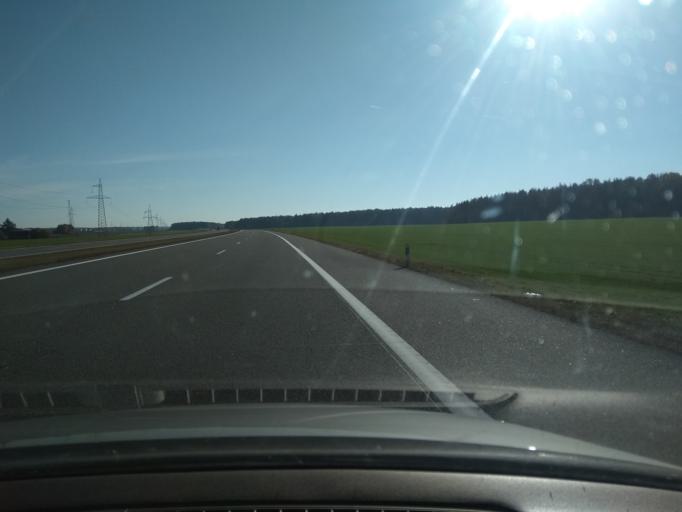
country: BY
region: Brest
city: Baranovichi
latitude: 53.0984
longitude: 25.8865
